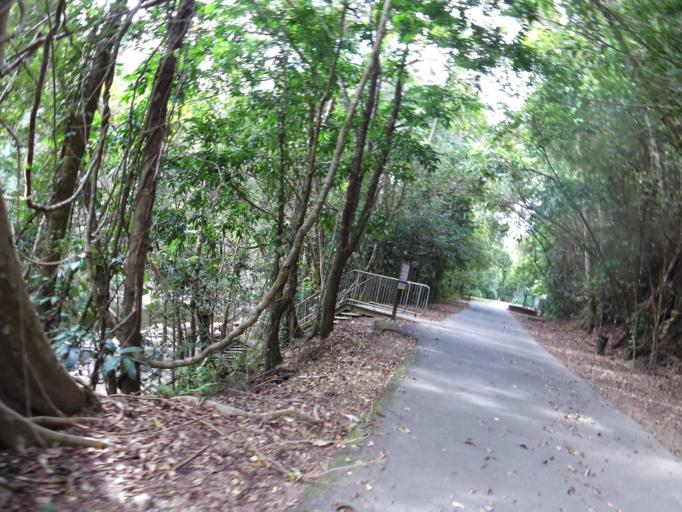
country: AU
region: Queensland
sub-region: Cairns
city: Woree
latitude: -16.9636
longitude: 145.6773
